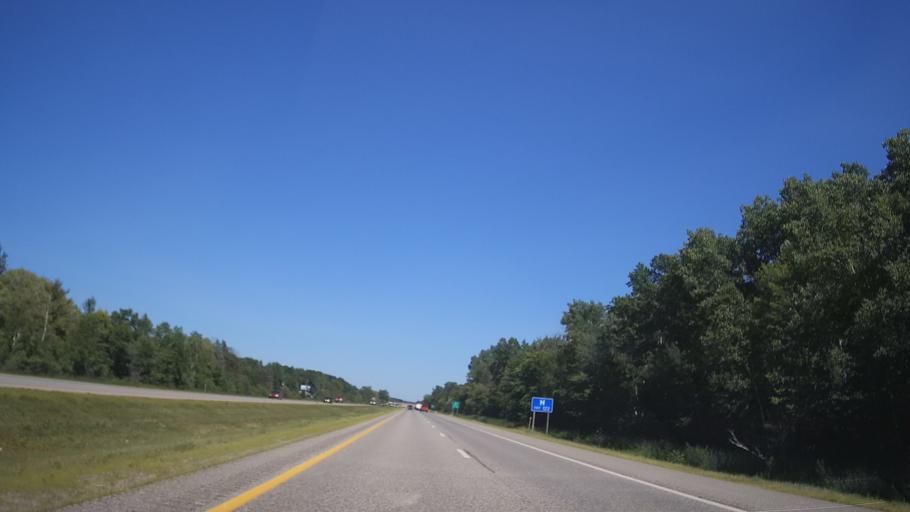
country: US
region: Michigan
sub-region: Midland County
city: Midland
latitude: 43.6560
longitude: -84.2837
